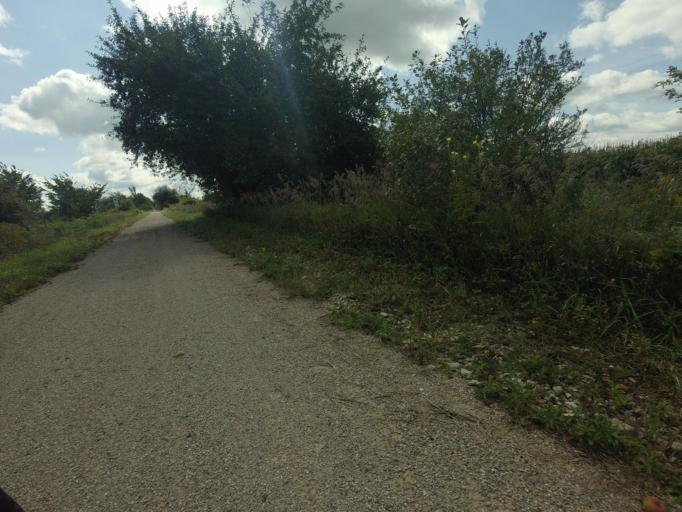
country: CA
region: Ontario
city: Huron East
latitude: 43.6569
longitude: -81.2429
